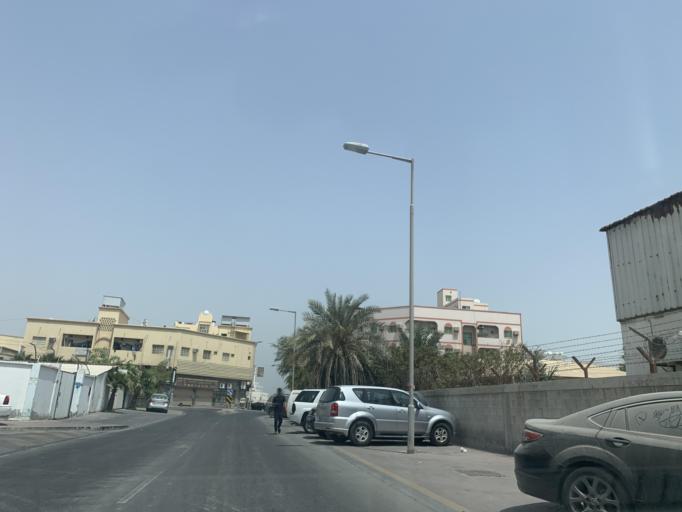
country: BH
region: Northern
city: Madinat `Isa
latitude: 26.1883
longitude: 50.5533
